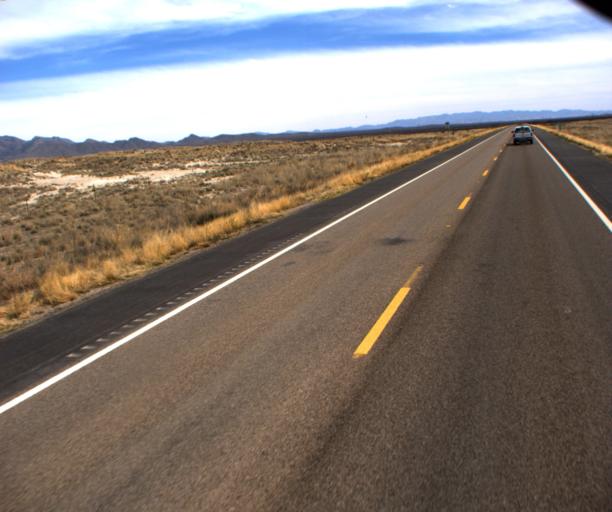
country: US
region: Arizona
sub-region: Cochise County
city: Willcox
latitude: 32.2065
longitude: -109.7731
